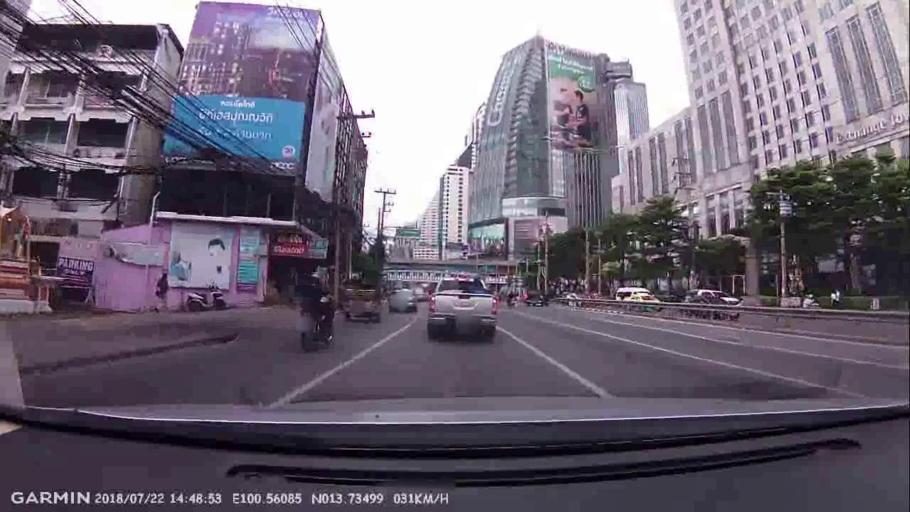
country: TH
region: Bangkok
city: Khlong Toei
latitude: 13.7349
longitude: 100.5607
